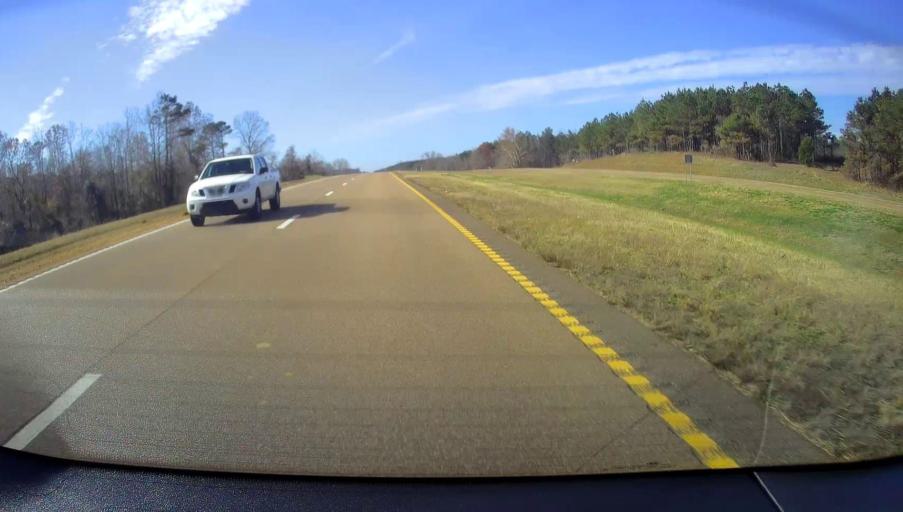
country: US
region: Mississippi
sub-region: Benton County
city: Ashland
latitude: 34.9492
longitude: -89.0963
